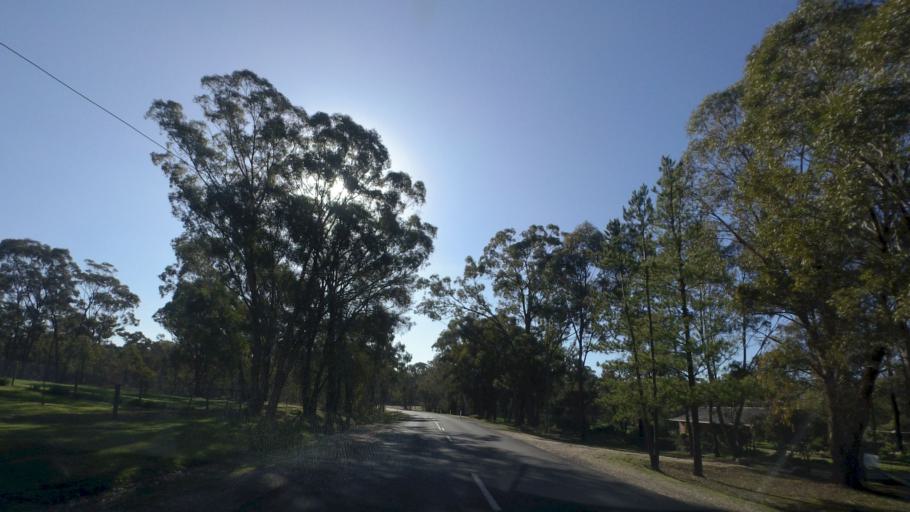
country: AU
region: Victoria
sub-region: Greater Bendigo
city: Kangaroo Flat
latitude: -36.8269
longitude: 144.2769
